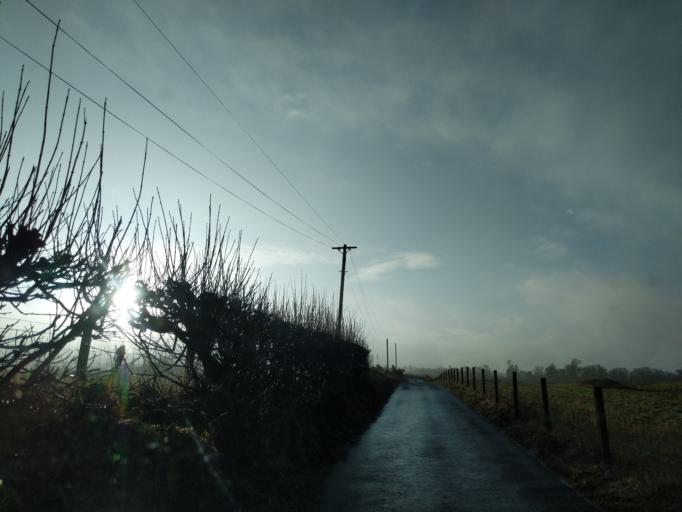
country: GB
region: Scotland
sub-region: Perth and Kinross
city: Auchterarder
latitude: 56.2925
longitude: -3.6917
